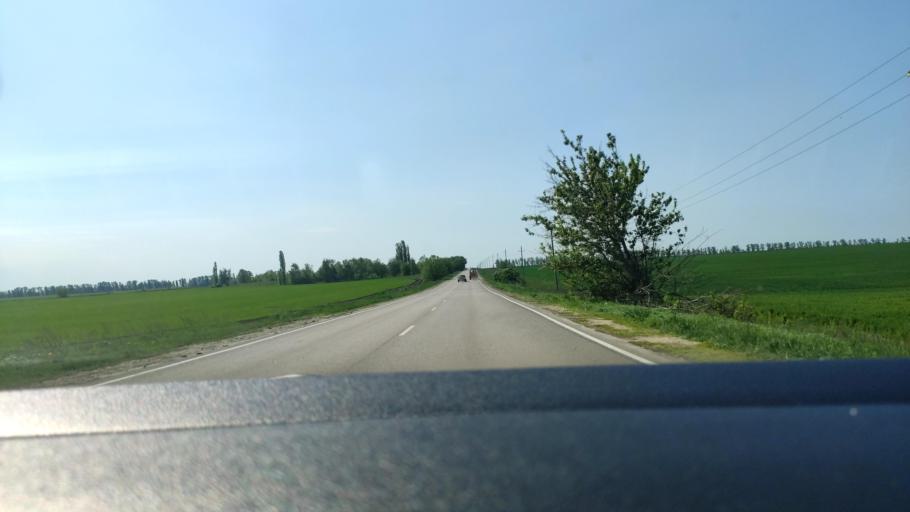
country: RU
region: Voronezj
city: Novaya Usman'
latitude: 51.5769
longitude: 39.3750
